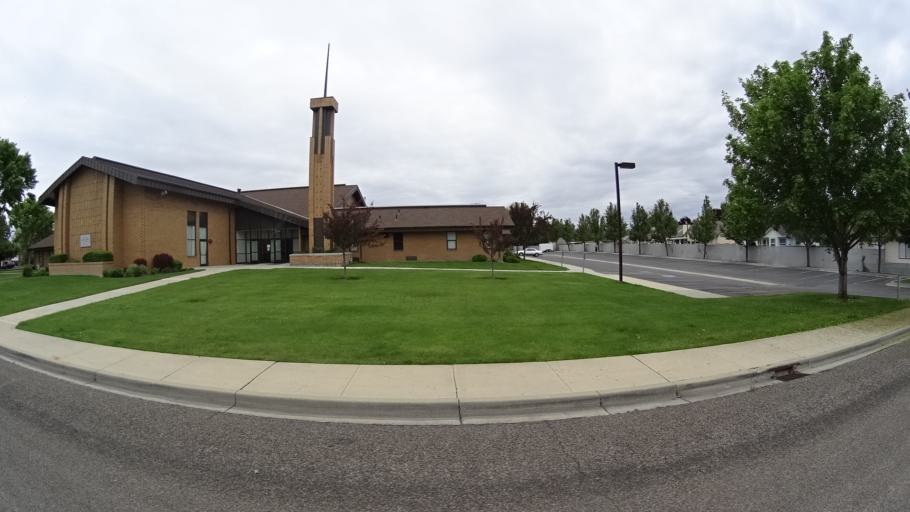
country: US
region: Idaho
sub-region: Ada County
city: Eagle
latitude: 43.6485
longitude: -116.3254
